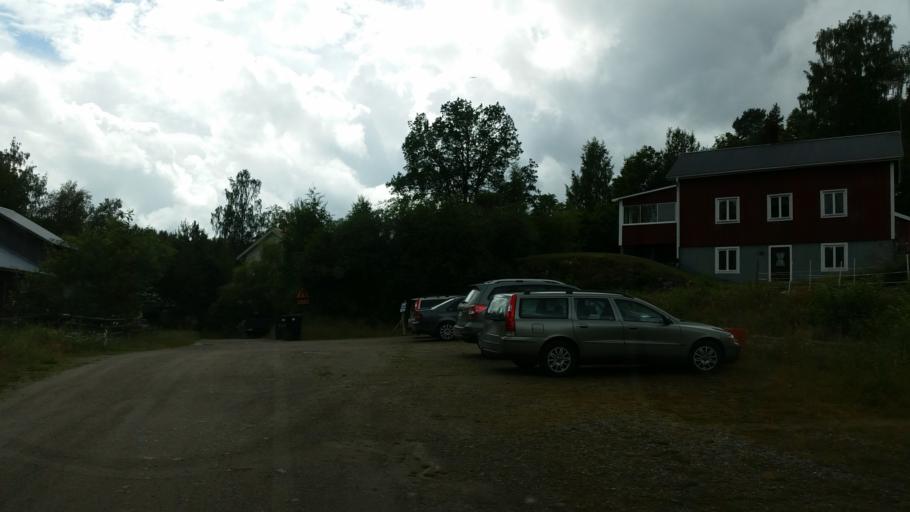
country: SE
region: Gaevleborg
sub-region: Hudiksvalls Kommun
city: Delsbo
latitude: 61.8097
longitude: 16.5516
